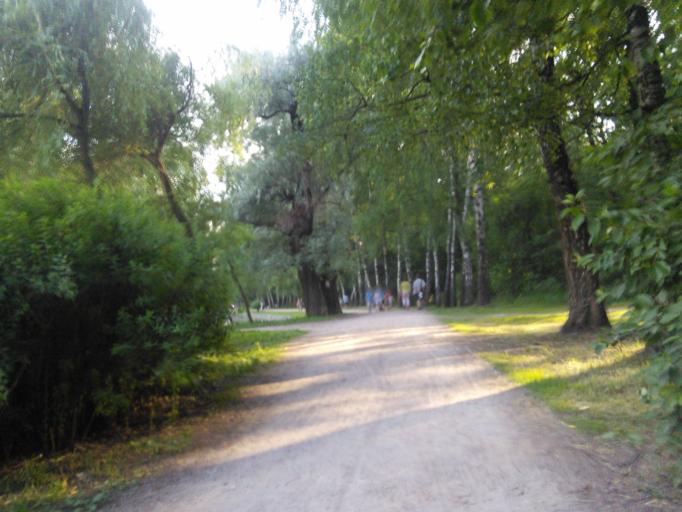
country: RU
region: Moscow
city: Sokol'niki
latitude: 55.8141
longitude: 37.6716
